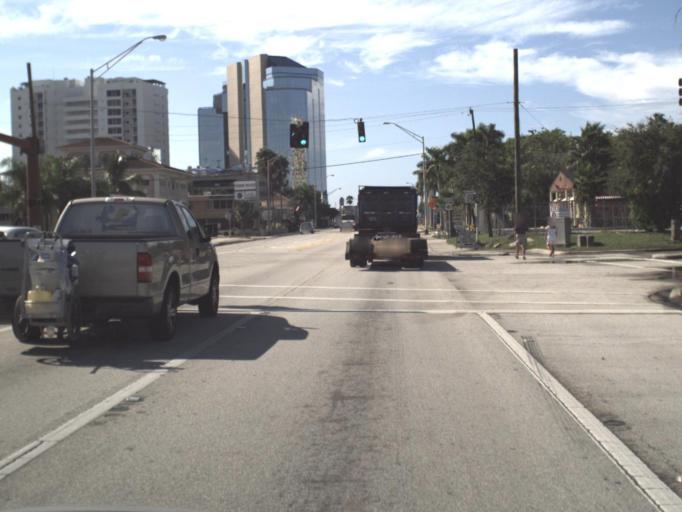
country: US
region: Florida
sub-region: Sarasota County
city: Sarasota
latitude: 27.3392
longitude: -82.5469
